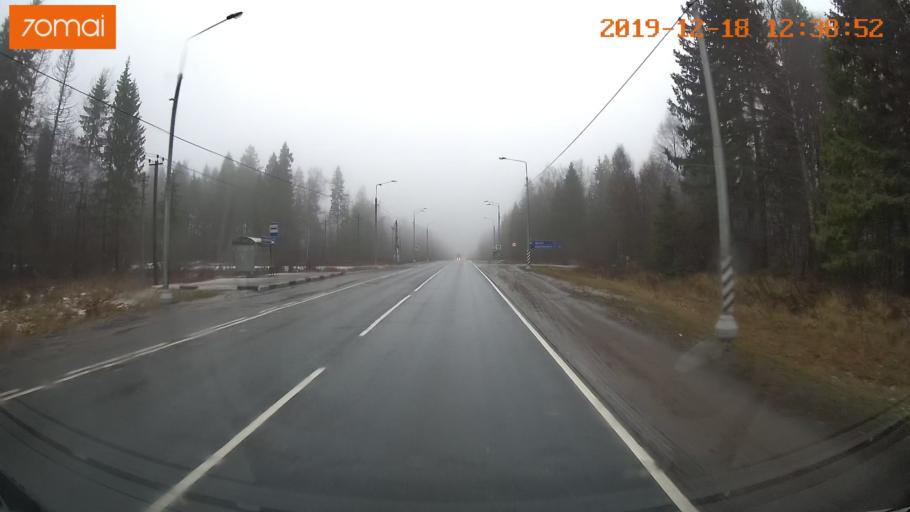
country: RU
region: Moskovskaya
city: Vysokovsk
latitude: 56.1574
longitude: 36.6077
